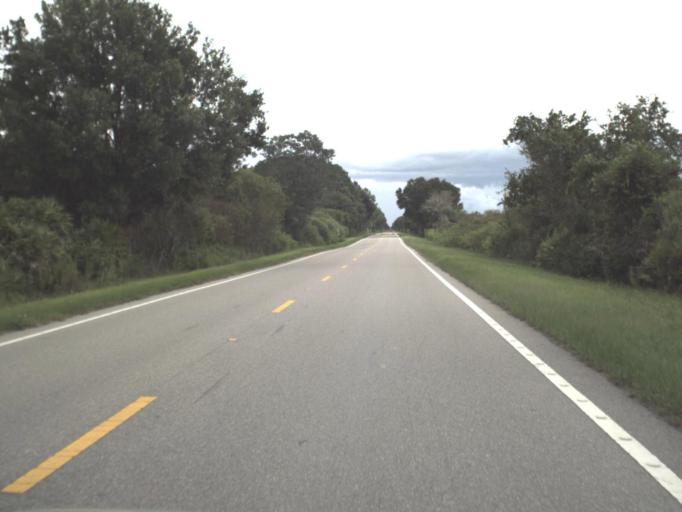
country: US
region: Florida
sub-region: Hillsborough County
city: Balm
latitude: 27.6188
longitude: -82.0862
